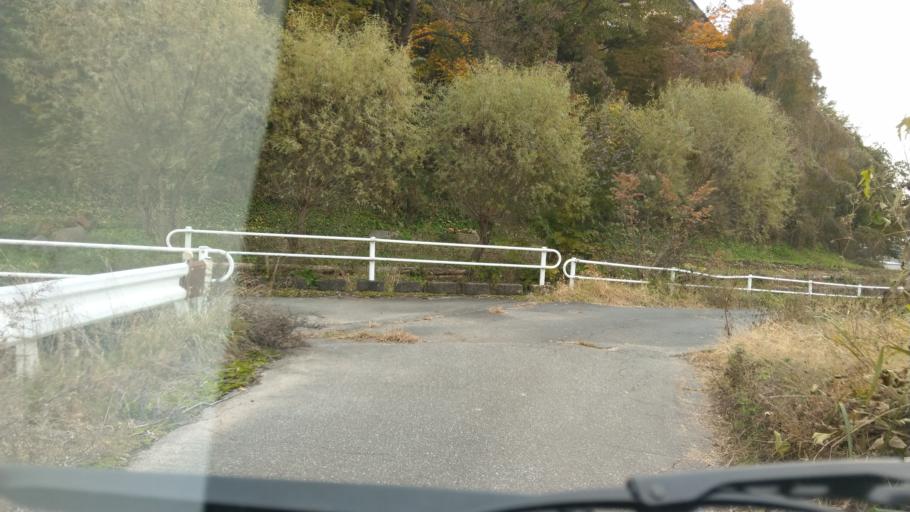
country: JP
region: Nagano
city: Komoro
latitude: 36.3158
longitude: 138.4582
